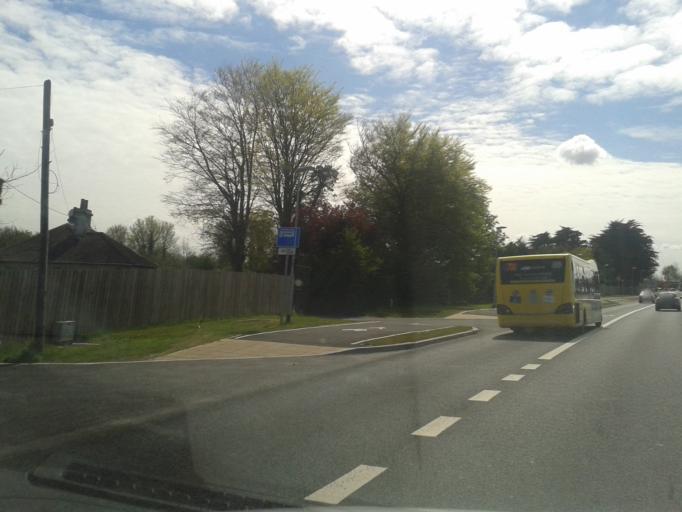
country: IE
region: Leinster
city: Beaumont
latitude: 53.4204
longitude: -6.2334
